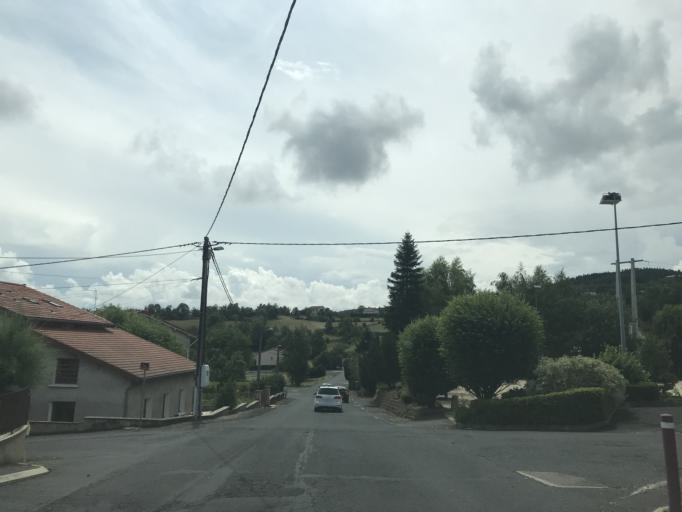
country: FR
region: Auvergne
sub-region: Departement de la Haute-Loire
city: Cussac-sur-Loire
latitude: 44.9913
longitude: 3.8687
